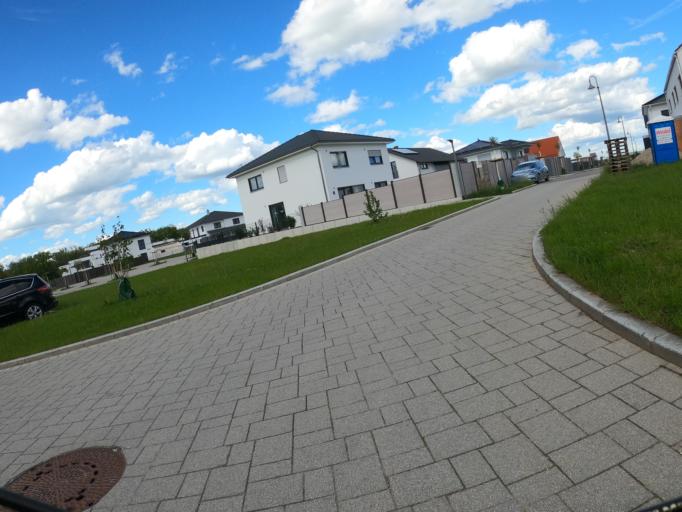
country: DE
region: Bavaria
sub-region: Swabia
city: Leipheim
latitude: 48.4505
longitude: 10.2338
